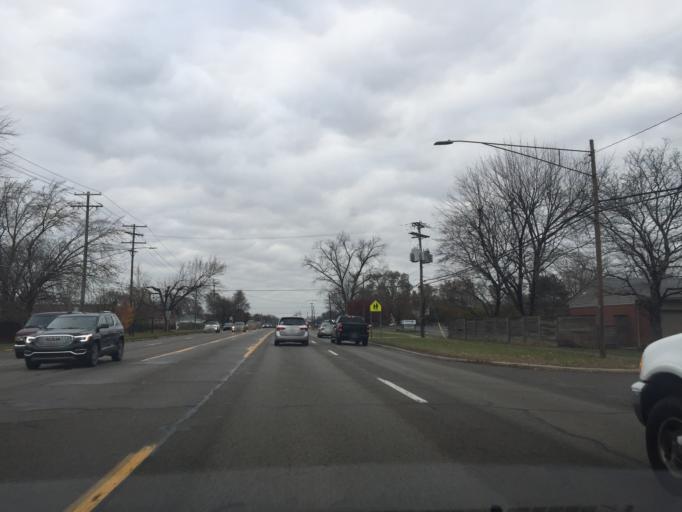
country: US
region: Michigan
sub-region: Wayne County
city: Livonia
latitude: 42.3920
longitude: -83.3341
